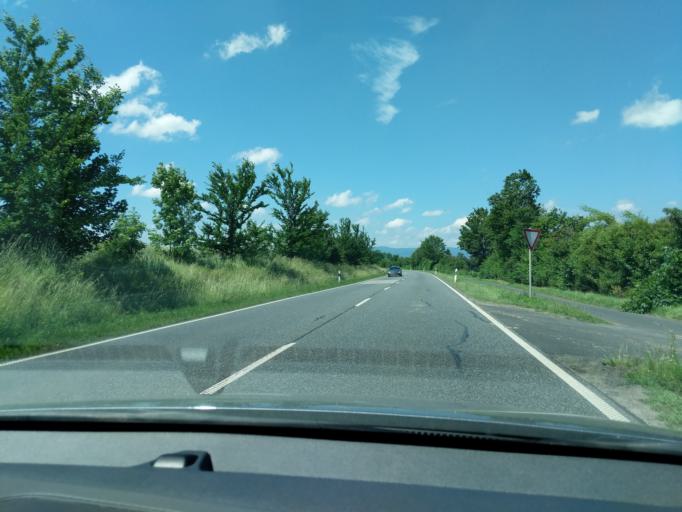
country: DE
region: Hesse
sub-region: Regierungsbezirk Darmstadt
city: Bad Vilbel
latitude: 50.1912
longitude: 8.7637
